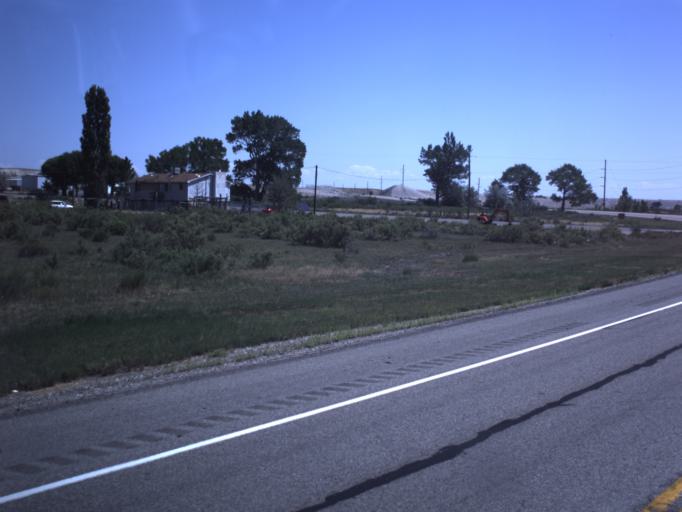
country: US
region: Utah
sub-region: Emery County
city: Ferron
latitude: 38.9232
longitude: -111.2444
